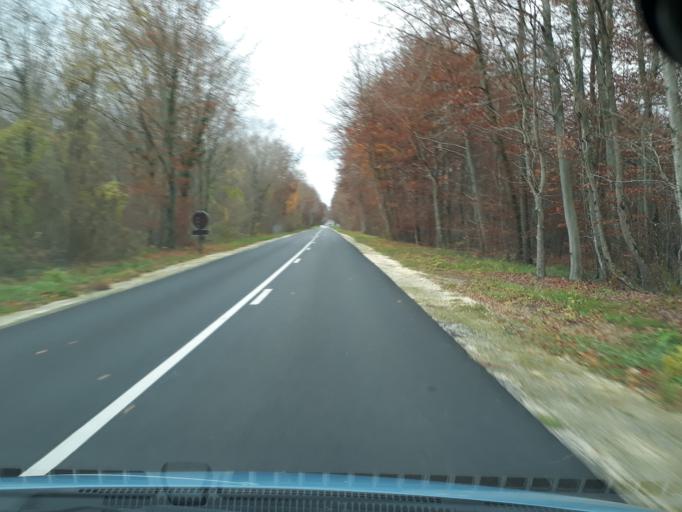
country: FR
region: Ile-de-France
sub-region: Departement de Seine-et-Marne
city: Thomery
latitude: 48.3947
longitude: 2.7678
